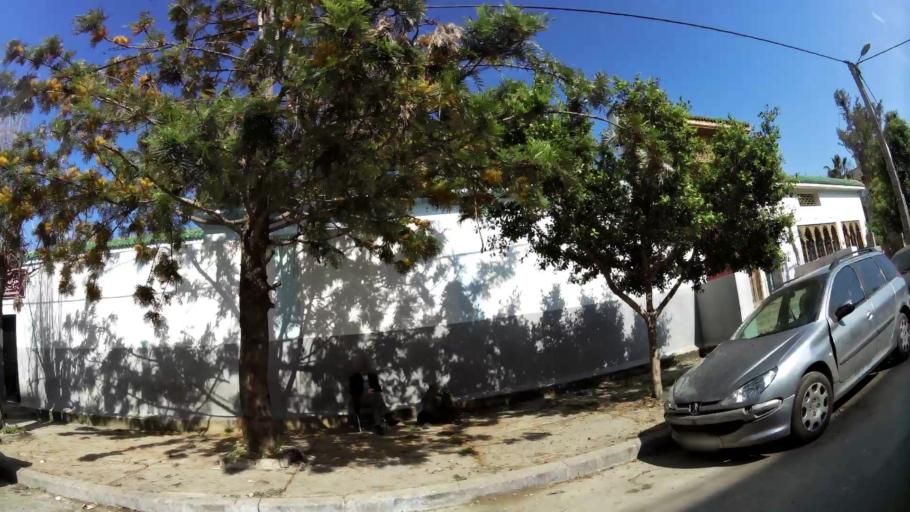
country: MA
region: Rabat-Sale-Zemmour-Zaer
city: Sale
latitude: 34.0453
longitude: -6.7824
